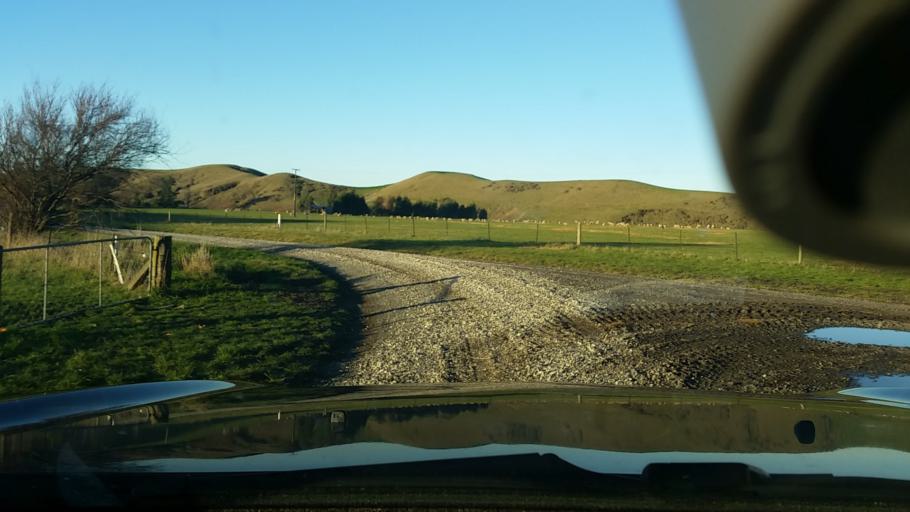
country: NZ
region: Marlborough
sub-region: Marlborough District
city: Blenheim
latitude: -41.7485
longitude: 174.0748
